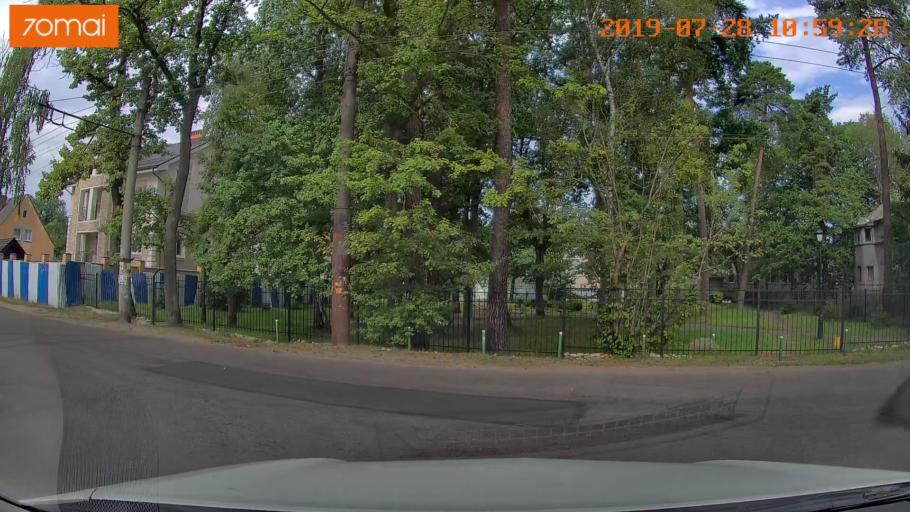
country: RU
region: Kaliningrad
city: Vzmorye
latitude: 54.7284
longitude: 20.3569
